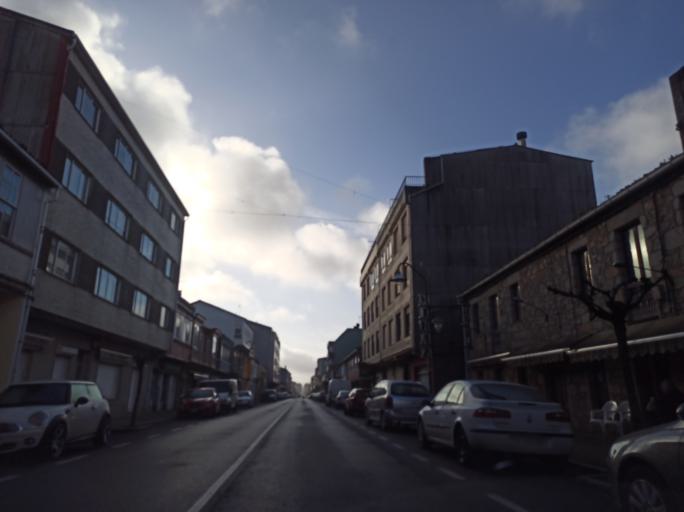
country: ES
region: Galicia
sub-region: Provincia da Coruna
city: Curtis
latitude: 43.1406
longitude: -8.0370
